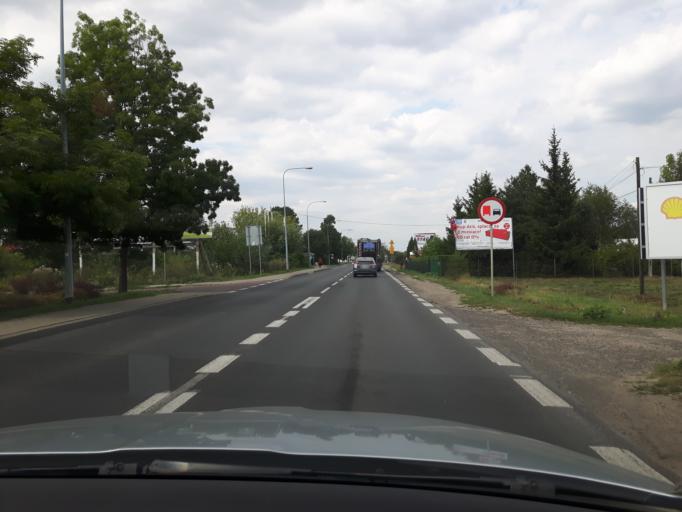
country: PL
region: Masovian Voivodeship
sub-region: Powiat legionowski
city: Stanislawow Pierwszy
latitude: 52.3379
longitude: 21.0292
